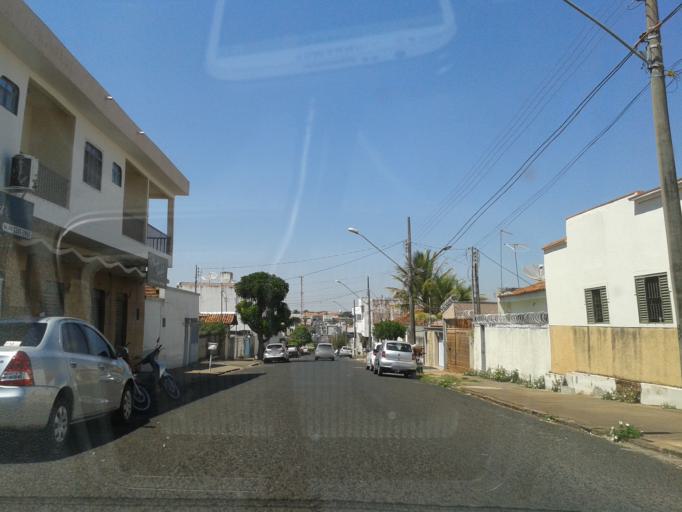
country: BR
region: Minas Gerais
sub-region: Araguari
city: Araguari
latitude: -18.6494
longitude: -48.1971
